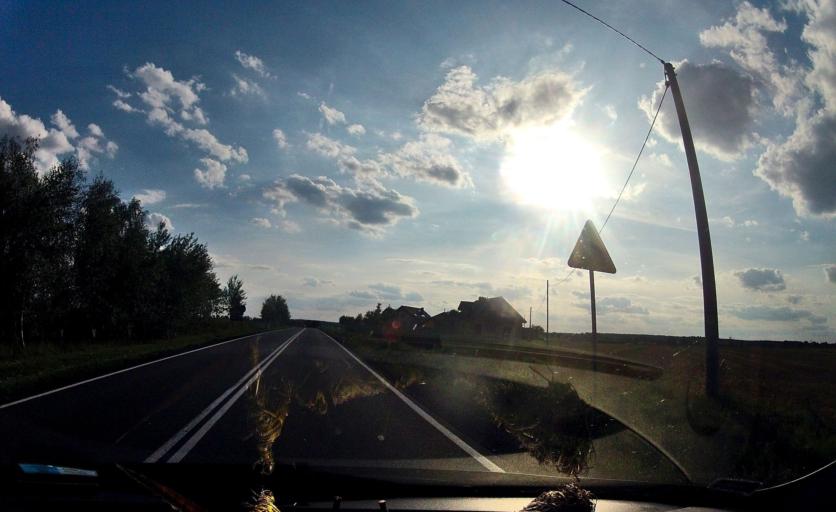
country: PL
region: Opole Voivodeship
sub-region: Powiat oleski
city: Praszka
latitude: 51.0537
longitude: 18.4321
